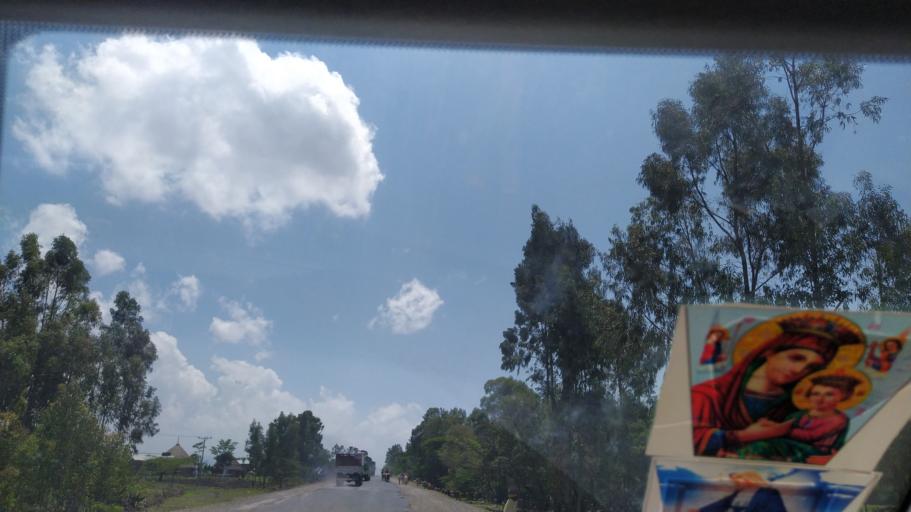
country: ET
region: Southern Nations, Nationalities, and People's Region
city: Butajira
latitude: 7.7608
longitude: 38.1332
